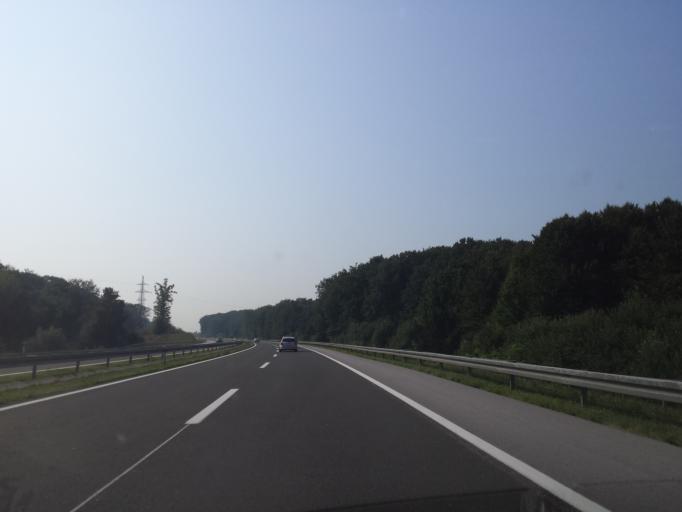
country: HR
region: Karlovacka
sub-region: Grad Ogulin
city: Ogulin
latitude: 45.3672
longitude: 15.2705
